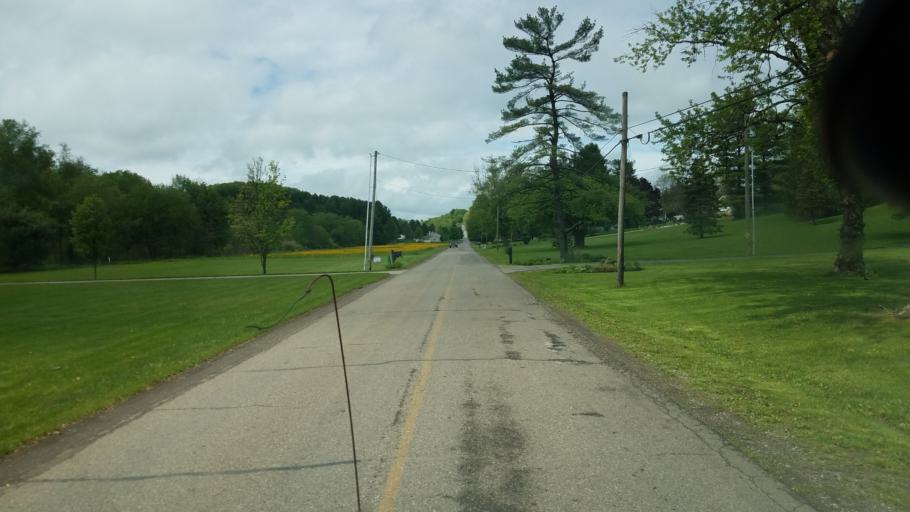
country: US
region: Ohio
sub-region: Tuscarawas County
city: New Philadelphia
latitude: 40.5096
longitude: -81.4178
